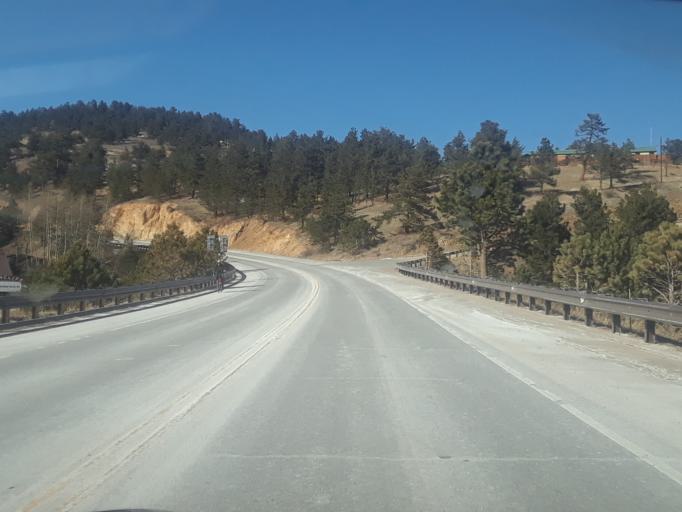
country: US
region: Colorado
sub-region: Larimer County
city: Estes Park
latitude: 40.1912
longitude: -105.5104
